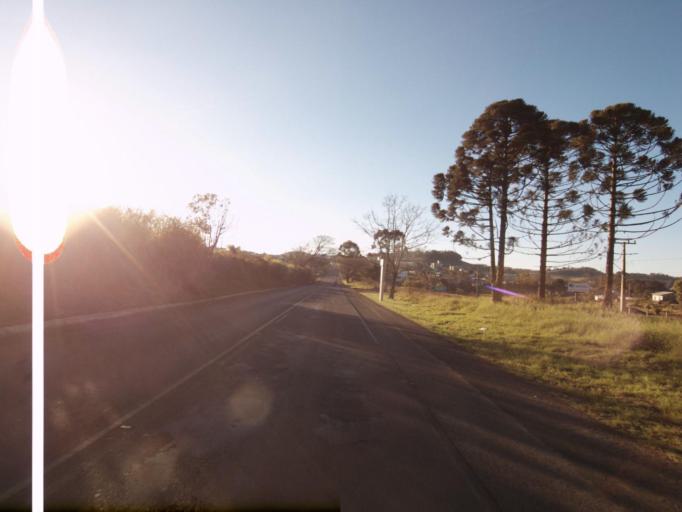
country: BR
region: Santa Catarina
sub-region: Chapeco
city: Chapeco
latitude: -26.8463
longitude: -52.9808
